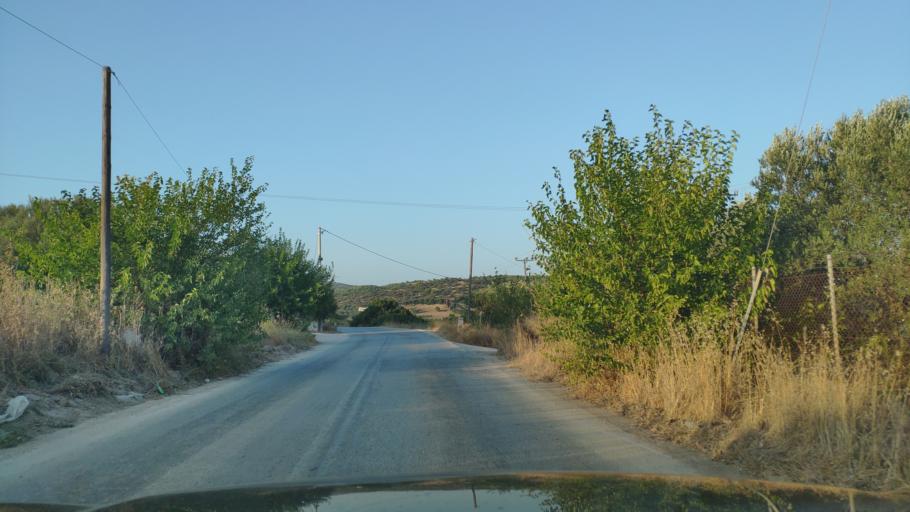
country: GR
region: Attica
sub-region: Nomarchia Anatolikis Attikis
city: Limin Mesoyaias
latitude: 37.9210
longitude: 23.9770
